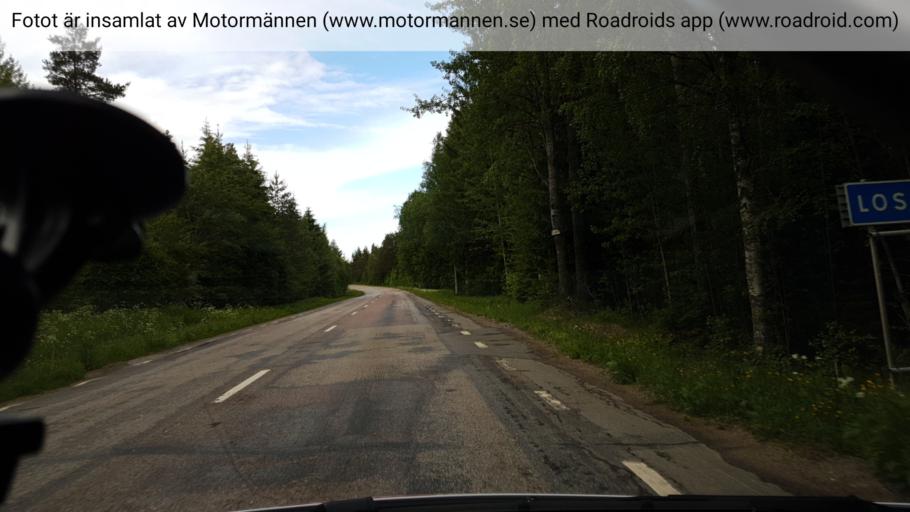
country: SE
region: Gaevleborg
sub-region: Soderhamns Kommun
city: Soderhamn
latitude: 61.4013
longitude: 16.9549
